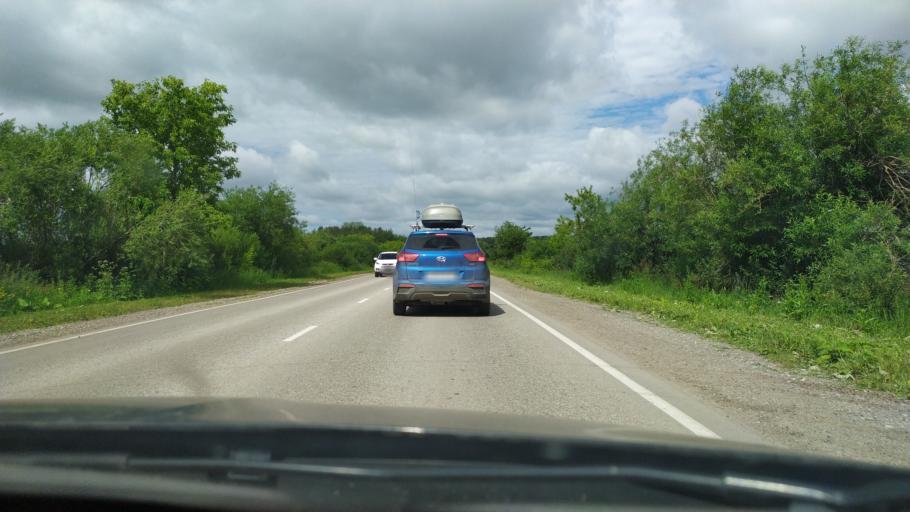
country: RU
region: Perm
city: Kondratovo
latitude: 57.9303
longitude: 56.0979
